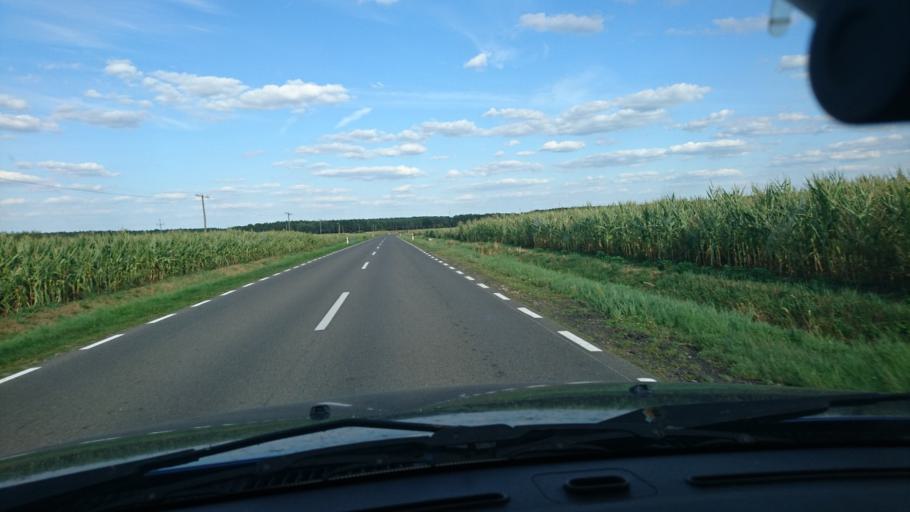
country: PL
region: Greater Poland Voivodeship
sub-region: Powiat krotoszynski
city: Sulmierzyce
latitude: 51.6051
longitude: 17.5580
